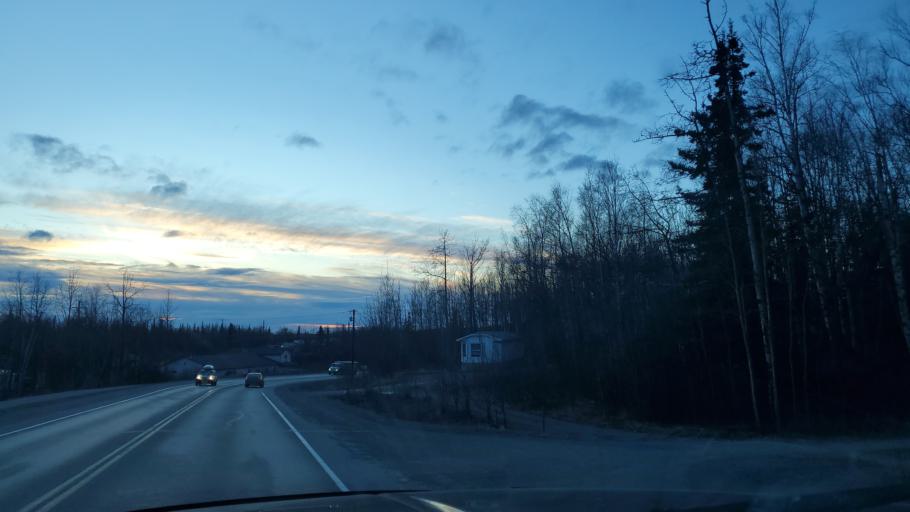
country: US
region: Alaska
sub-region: Matanuska-Susitna Borough
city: Wasilla
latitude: 61.5957
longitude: -149.4308
